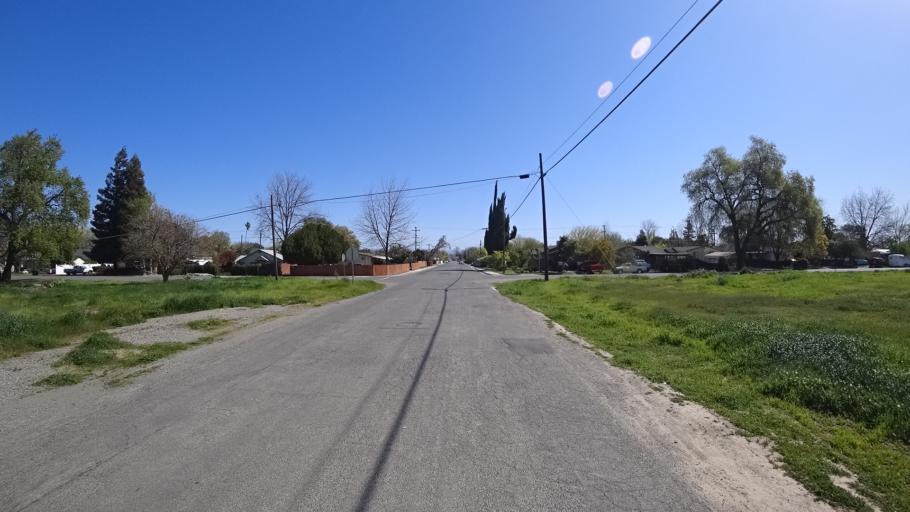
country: US
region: California
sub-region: Glenn County
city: Hamilton City
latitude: 39.7436
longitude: -122.0110
